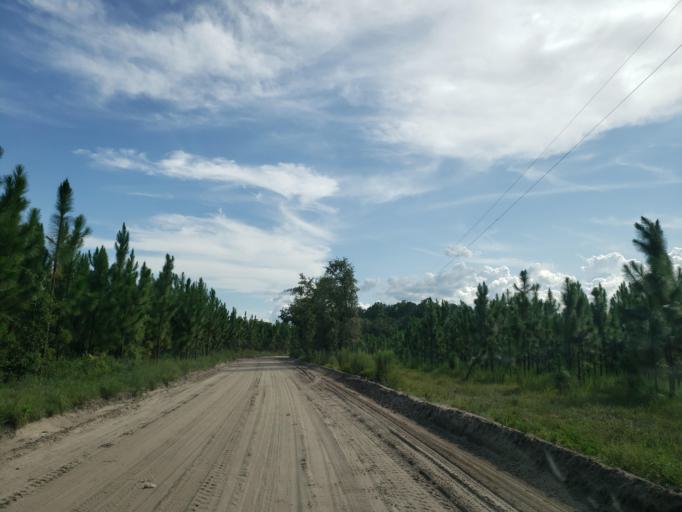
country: US
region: Georgia
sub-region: Echols County
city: Statenville
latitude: 30.6213
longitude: -83.2140
